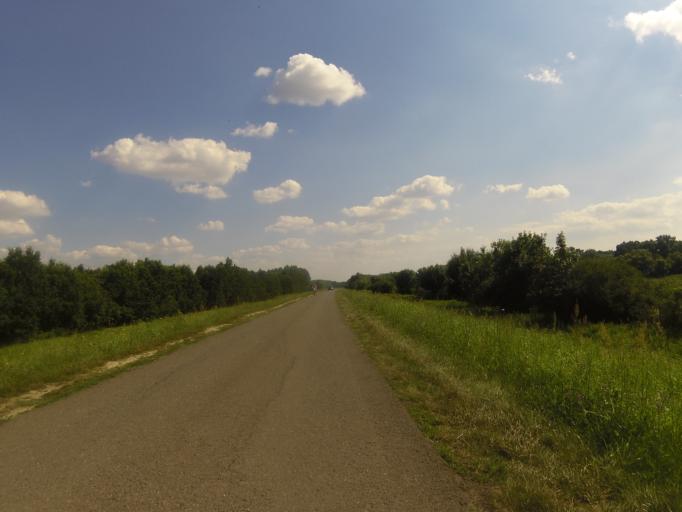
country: HU
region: Jasz-Nagykun-Szolnok
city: Tiszaszolos
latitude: 47.5939
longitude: 20.7107
